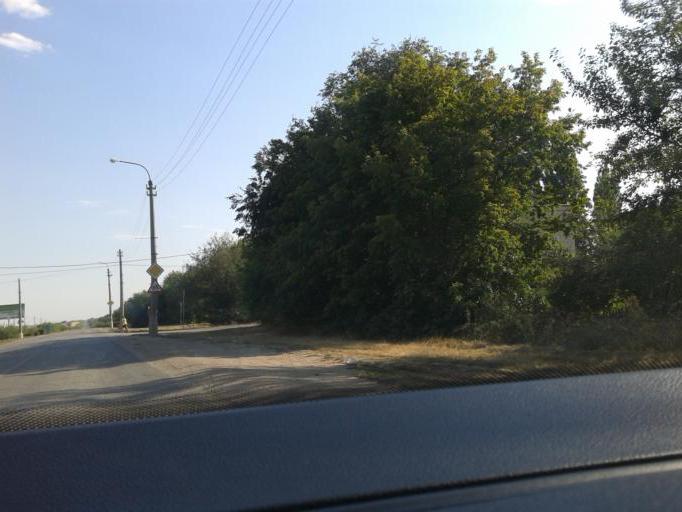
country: RU
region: Volgograd
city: Frolovo
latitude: 49.7502
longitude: 43.6539
